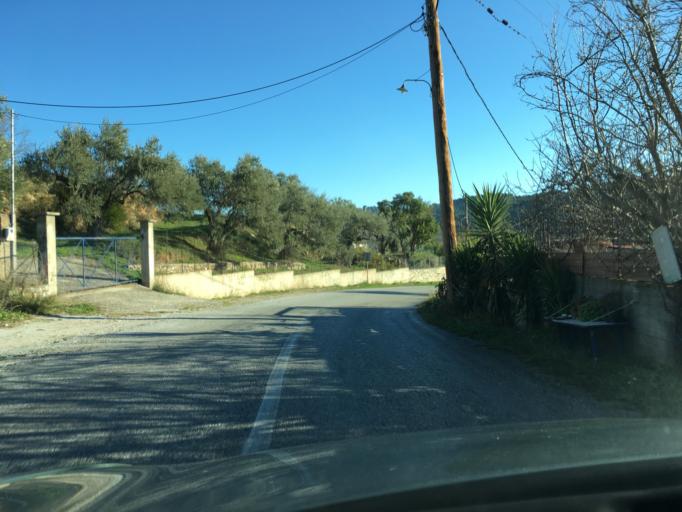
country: GR
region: Thessaly
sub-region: Nomos Magnisias
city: Skopelos
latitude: 39.0974
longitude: 23.6908
